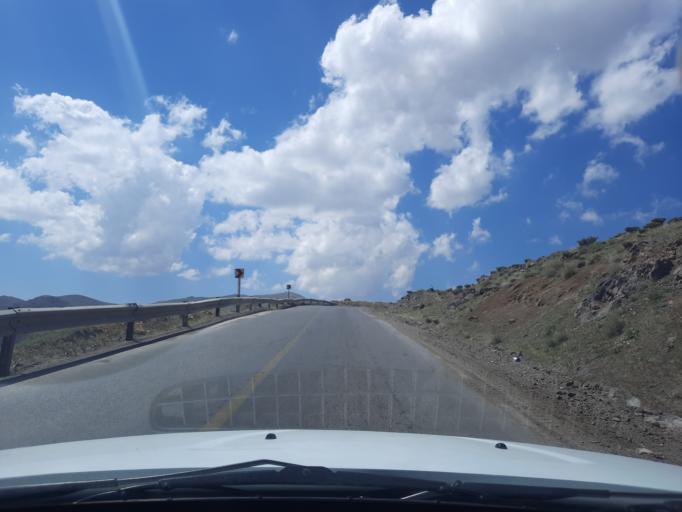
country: IR
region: Qazvin
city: Qazvin
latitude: 36.3697
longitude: 50.2005
